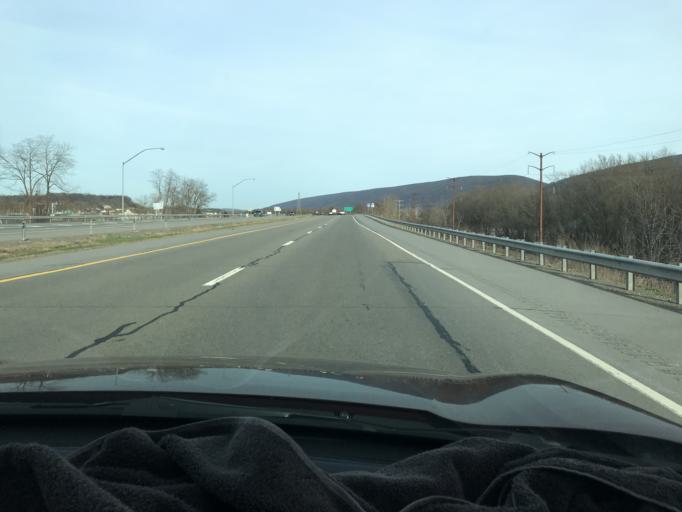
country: US
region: Pennsylvania
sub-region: Lycoming County
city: Faxon
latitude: 41.2479
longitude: -76.9736
